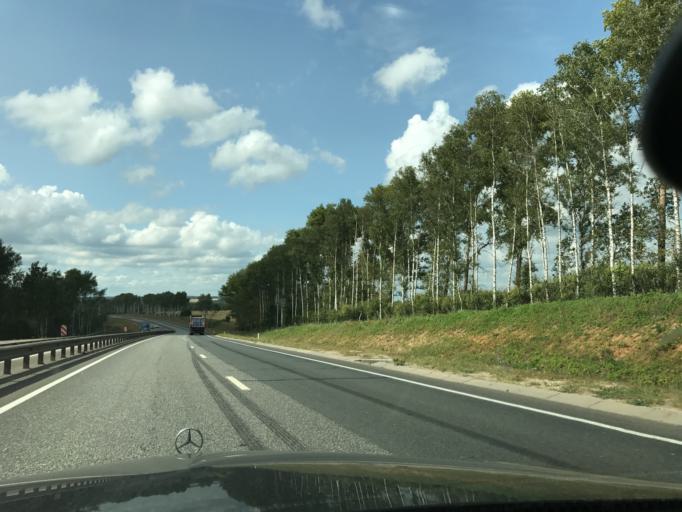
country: RU
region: Vladimir
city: Gorokhovets
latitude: 56.1632
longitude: 42.4968
